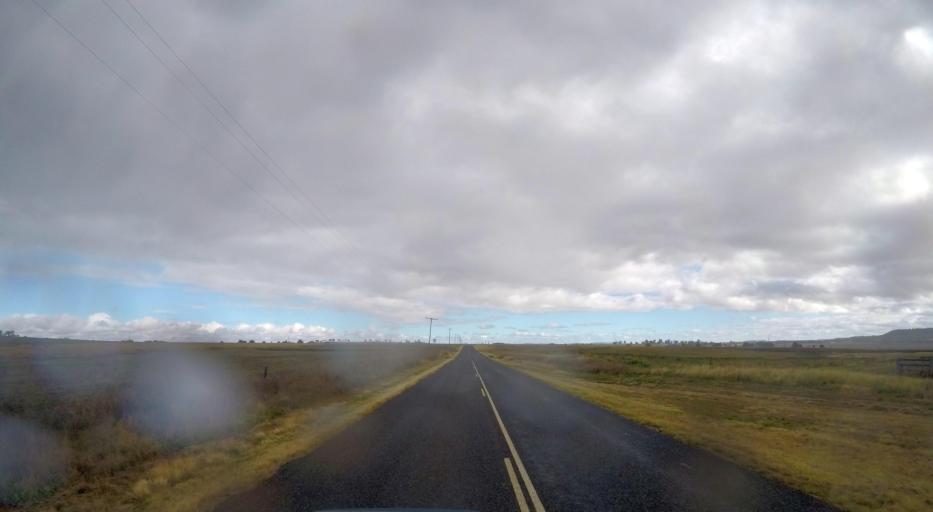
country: AU
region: Queensland
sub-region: Southern Downs
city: Warwick
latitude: -28.0520
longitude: 152.0317
